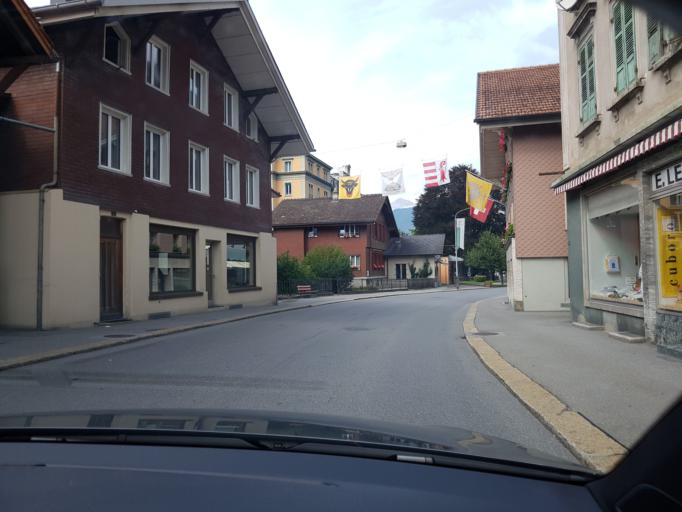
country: CH
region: Bern
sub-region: Interlaken-Oberhasli District
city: Meiringen
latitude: 46.7262
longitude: 8.1892
